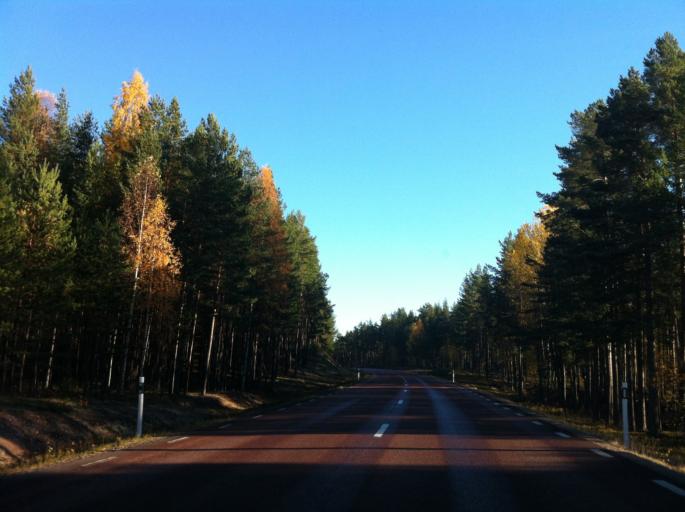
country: SE
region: Dalarna
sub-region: Leksand Municipality
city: Siljansnas
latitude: 60.9384
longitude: 14.7531
